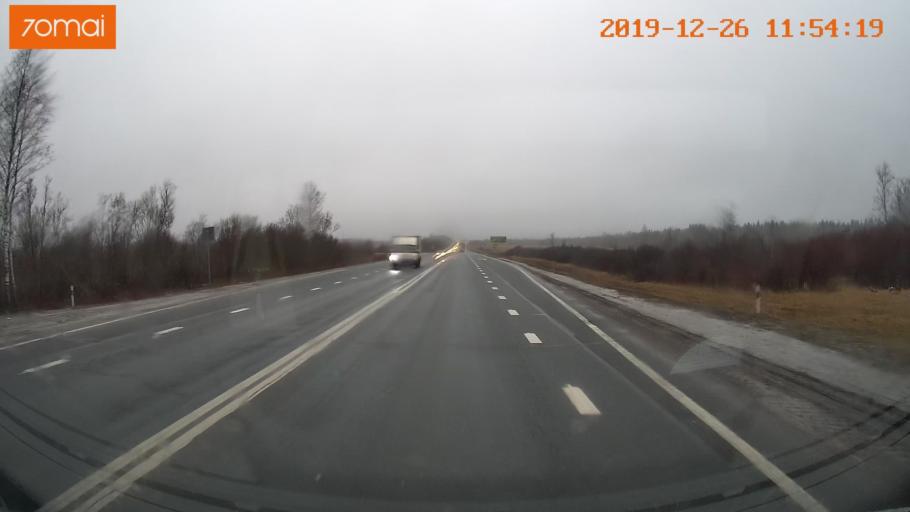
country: RU
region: Vologda
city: Sheksna
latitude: 59.2759
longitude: 38.3079
